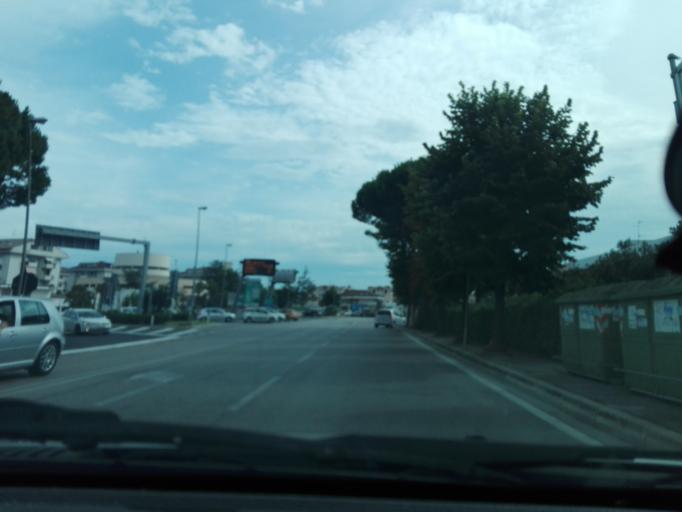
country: IT
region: Abruzzo
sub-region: Provincia di Pescara
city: San Martino Bassa
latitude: 42.5205
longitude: 14.1374
